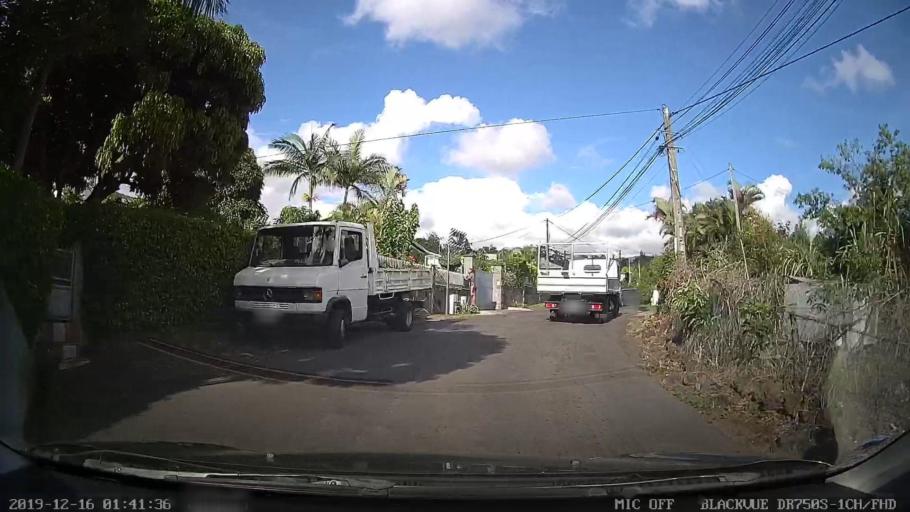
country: RE
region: Reunion
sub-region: Reunion
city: Le Tampon
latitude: -21.2554
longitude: 55.5093
